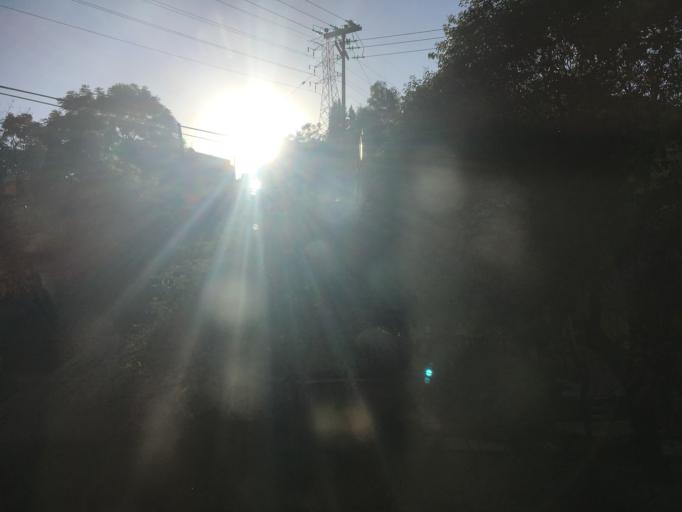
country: MX
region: Mexico City
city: Polanco
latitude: 19.3945
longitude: -99.2003
